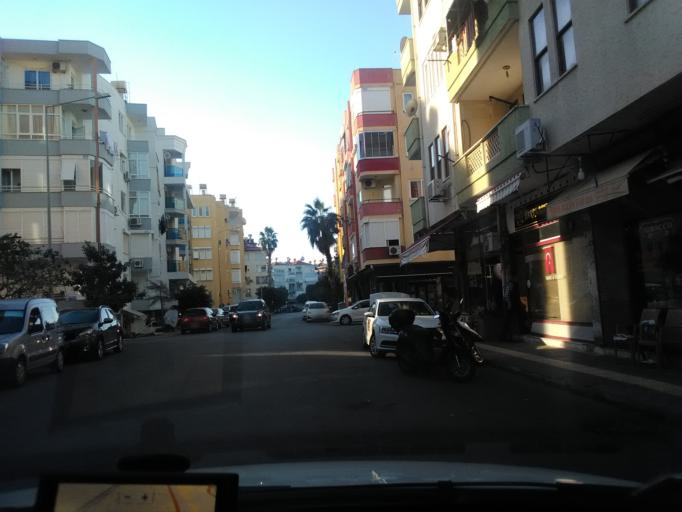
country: TR
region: Antalya
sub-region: Alanya
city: Alanya
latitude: 36.5451
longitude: 31.9900
